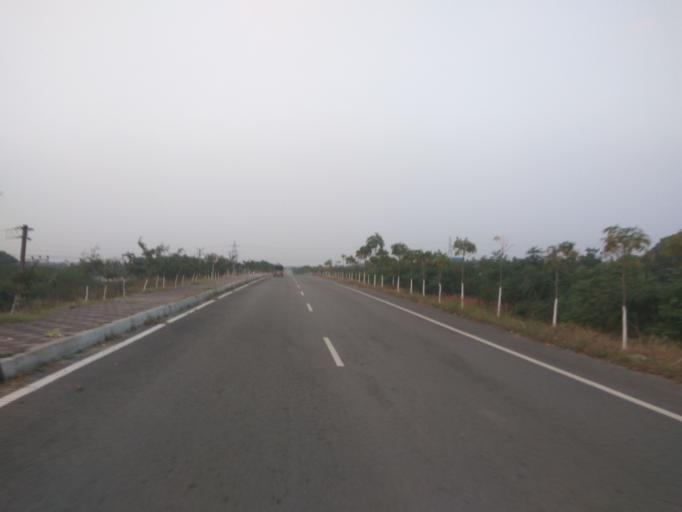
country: IN
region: Telangana
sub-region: Rangareddi
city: Secunderabad
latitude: 17.5450
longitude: 78.6301
